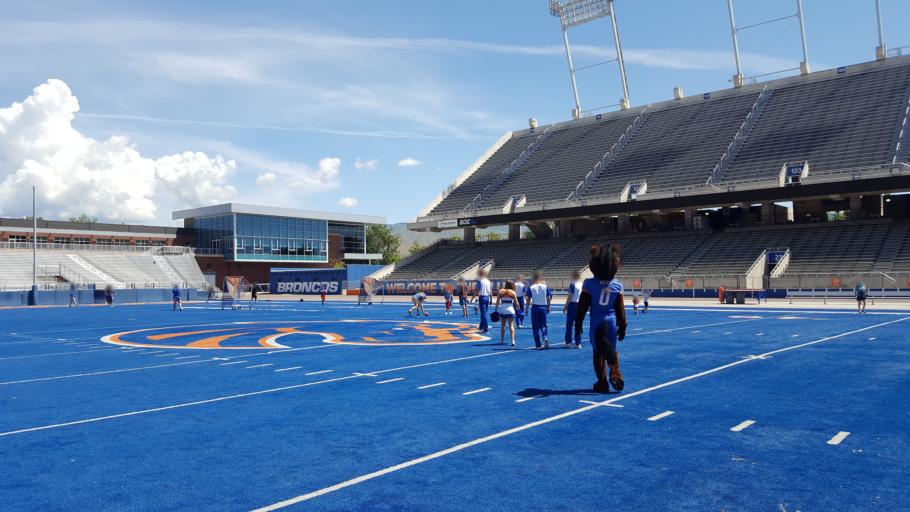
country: US
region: Idaho
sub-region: Ada County
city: Boise
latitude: 43.6025
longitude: -116.1972
